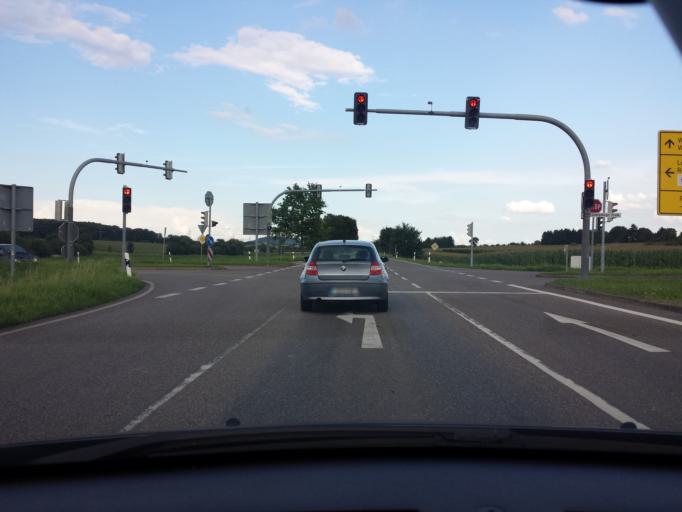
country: DE
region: Baden-Wuerttemberg
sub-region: Regierungsbezirk Stuttgart
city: Stuttgart Muehlhausen
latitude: 48.8476
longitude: 9.2689
